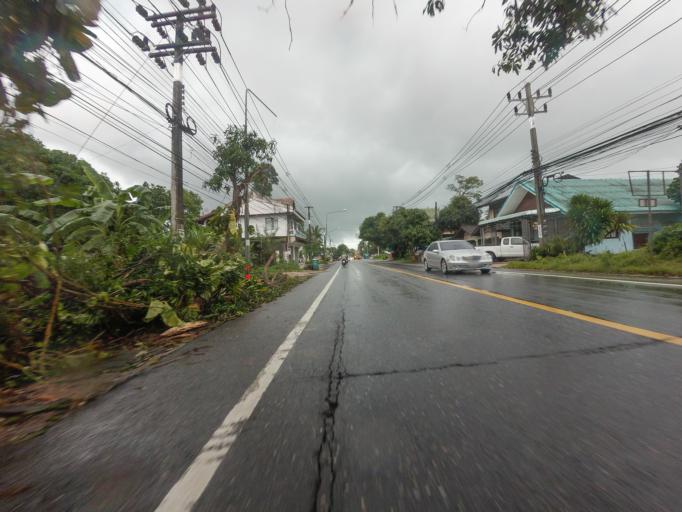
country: TH
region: Surat Thani
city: Ko Samui
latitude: 9.4433
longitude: 100.0140
